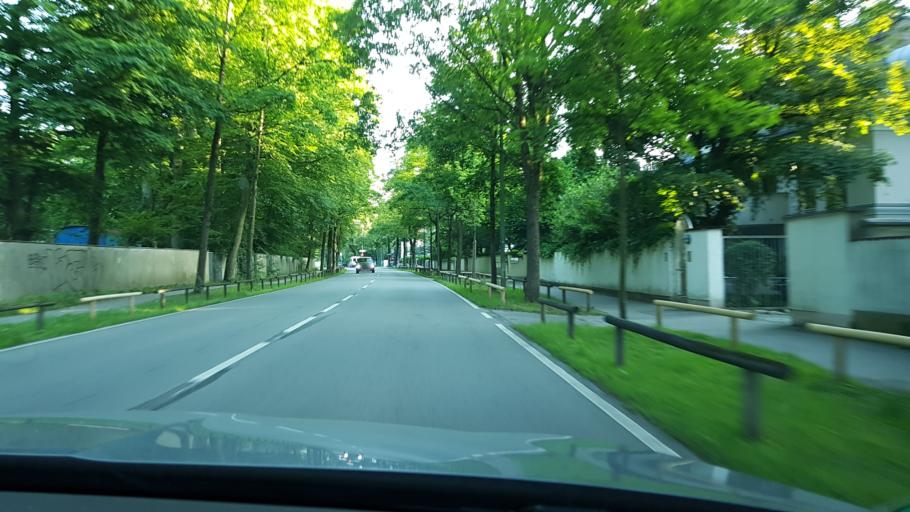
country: DE
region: Bavaria
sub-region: Upper Bavaria
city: Bogenhausen
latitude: 48.1659
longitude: 11.6231
